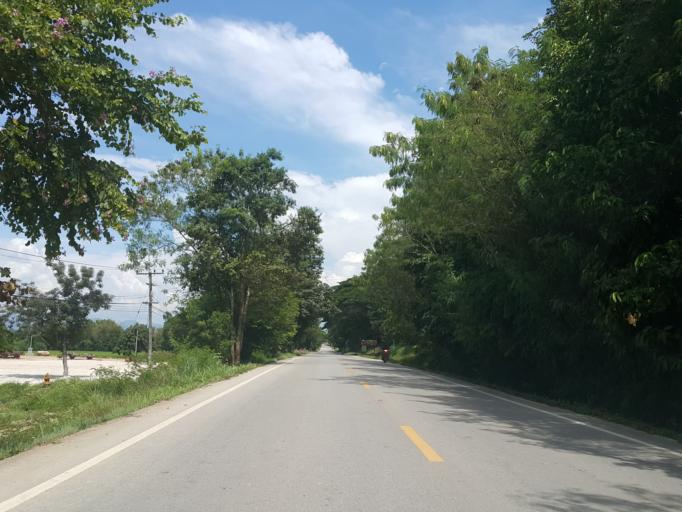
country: TH
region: Chiang Mai
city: Phrao
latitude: 19.2868
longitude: 99.1877
